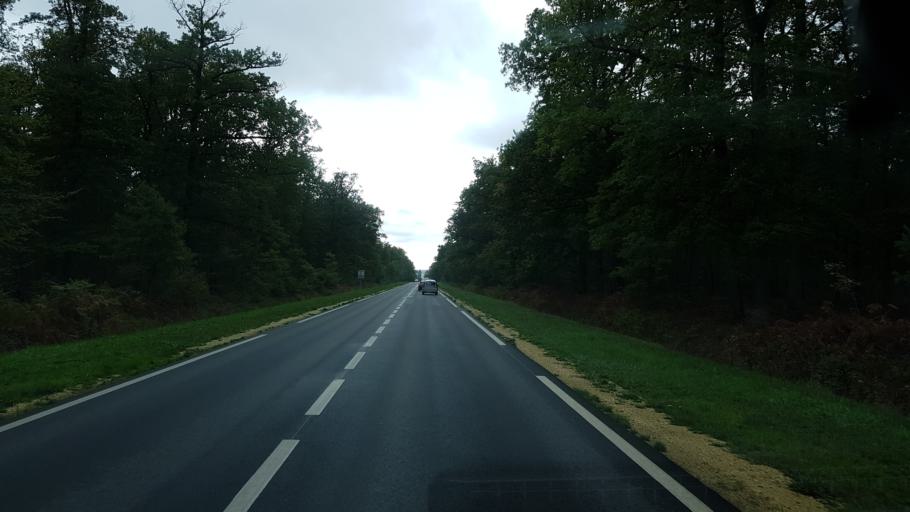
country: FR
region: Centre
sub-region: Departement du Cher
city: Vierzon
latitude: 47.2565
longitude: 2.0601
